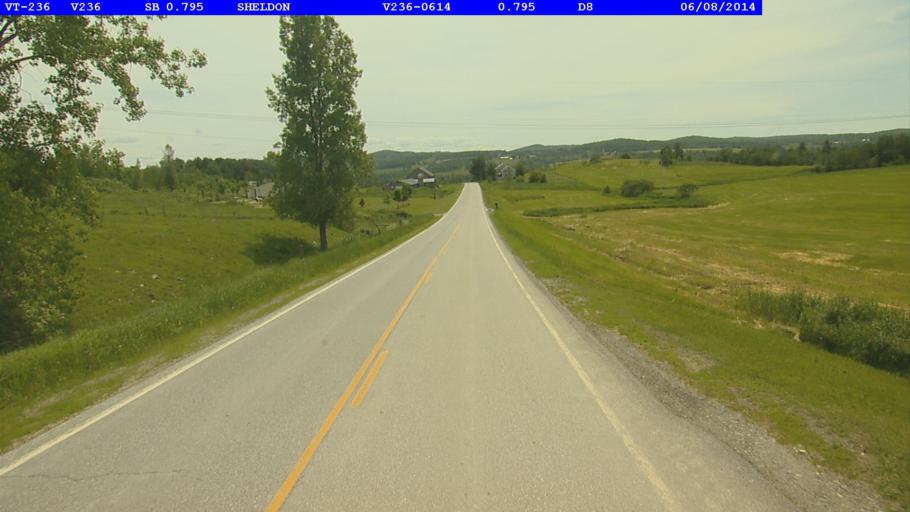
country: US
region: Vermont
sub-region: Franklin County
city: Enosburg Falls
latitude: 44.9223
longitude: -72.8653
